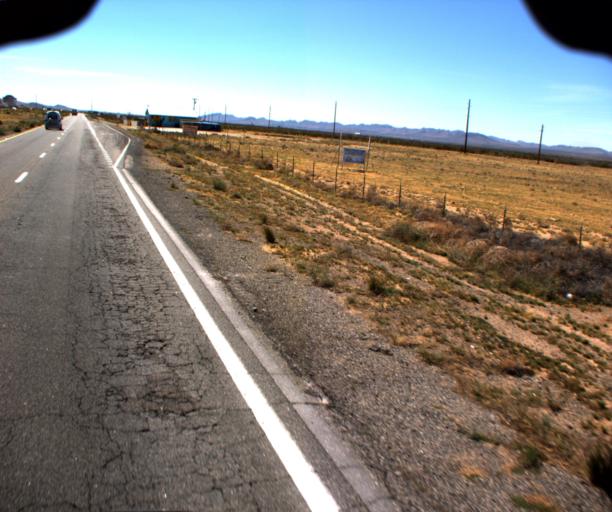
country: US
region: Arizona
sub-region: Mohave County
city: Dolan Springs
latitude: 35.5391
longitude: -114.3592
